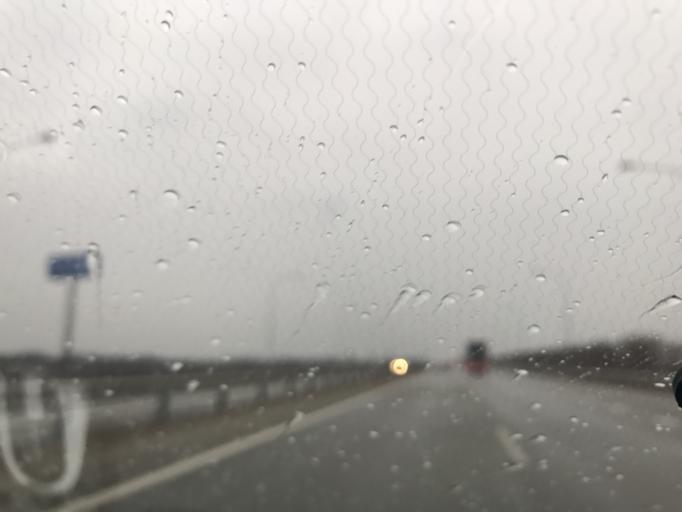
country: RU
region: Krasnodarskiy
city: Krylovskaya
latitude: 46.3032
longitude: 39.8127
